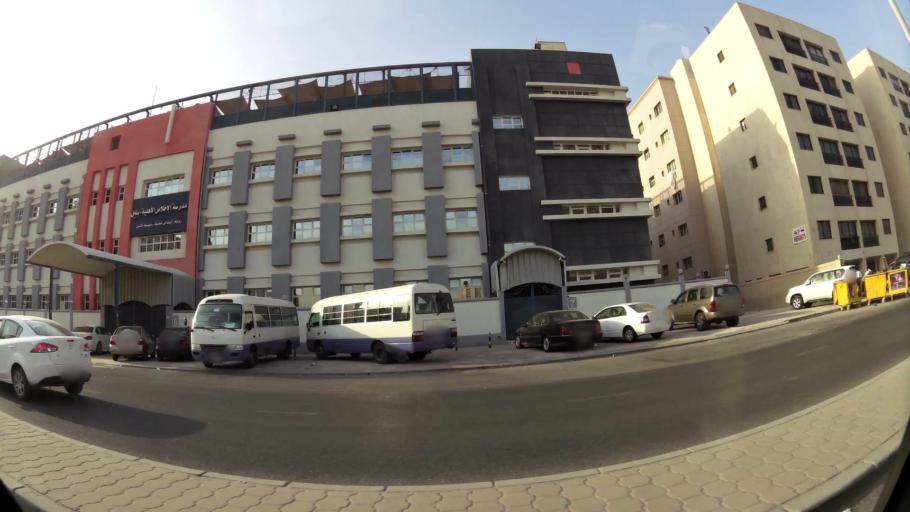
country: KW
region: Muhafazat Hawalli
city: Hawalli
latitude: 29.3281
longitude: 48.0505
